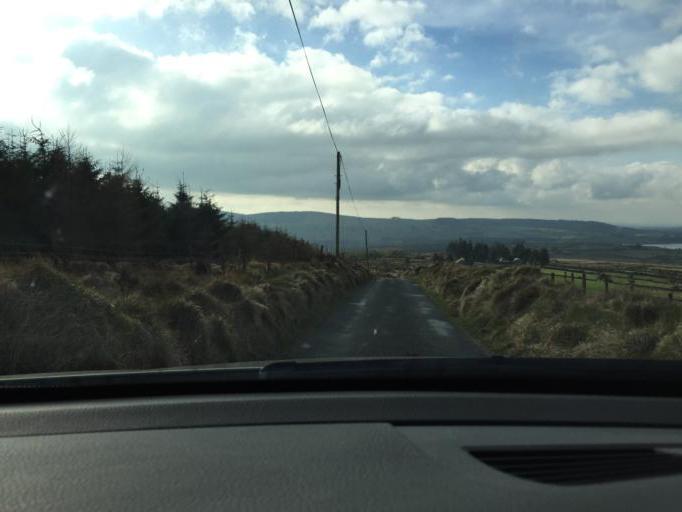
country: IE
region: Leinster
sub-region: Wicklow
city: Valleymount
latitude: 53.0745
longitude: -6.4993
